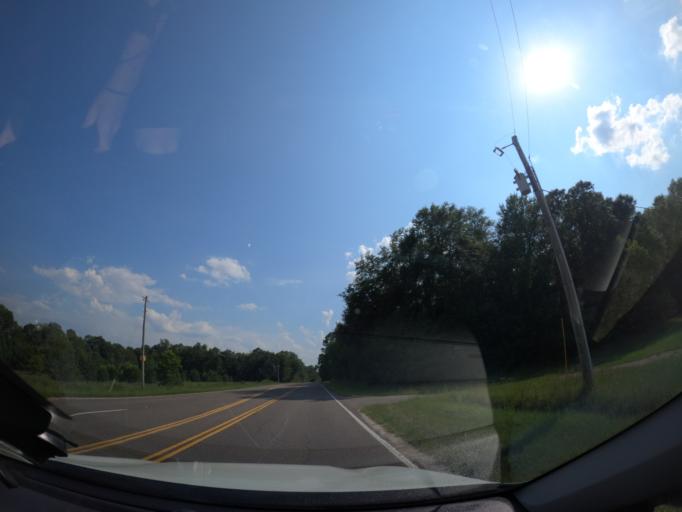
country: US
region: South Carolina
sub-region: Barnwell County
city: Williston
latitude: 33.5768
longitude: -81.4772
